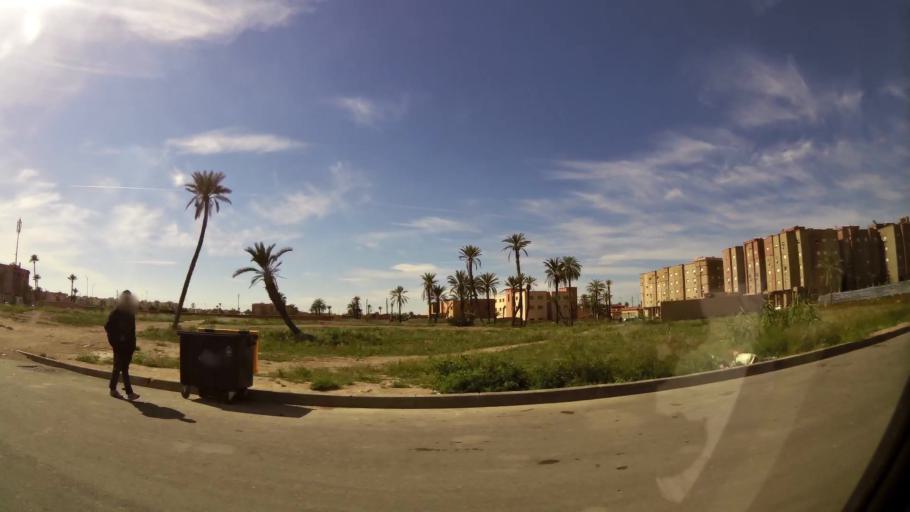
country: MA
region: Marrakech-Tensift-Al Haouz
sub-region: Marrakech
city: Marrakesh
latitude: 31.6596
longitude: -8.0236
